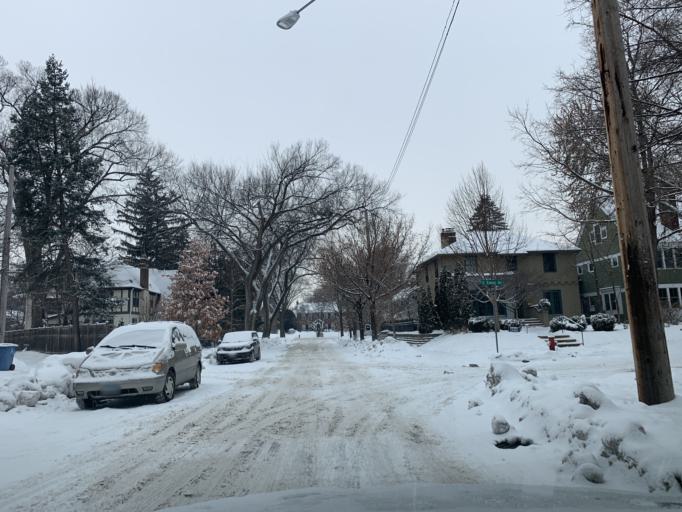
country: US
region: Minnesota
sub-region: Hennepin County
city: Saint Louis Park
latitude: 44.9513
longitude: -93.3273
